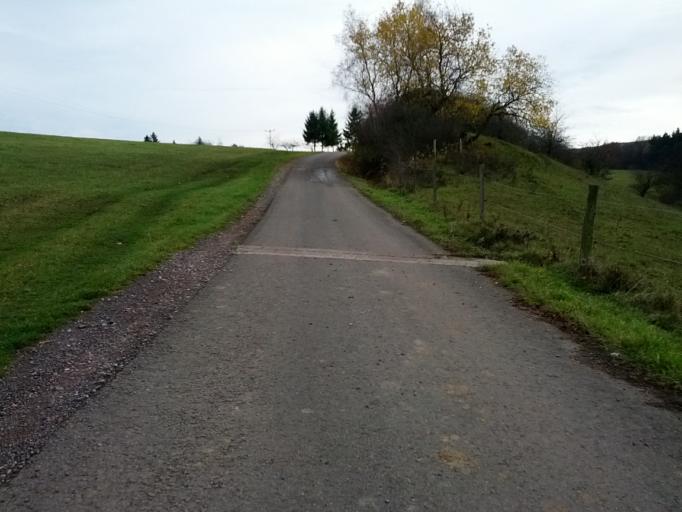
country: DE
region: Thuringia
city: Ruhla
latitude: 50.9346
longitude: 10.3470
